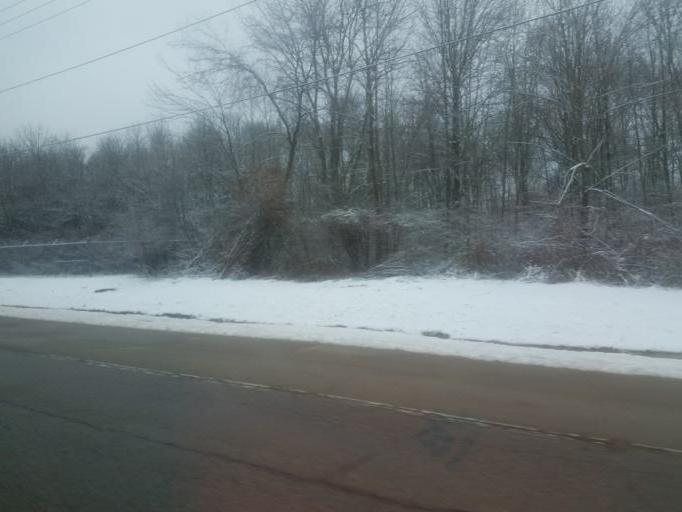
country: US
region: Ohio
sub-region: Geauga County
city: Middlefield
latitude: 41.4677
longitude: -81.0898
